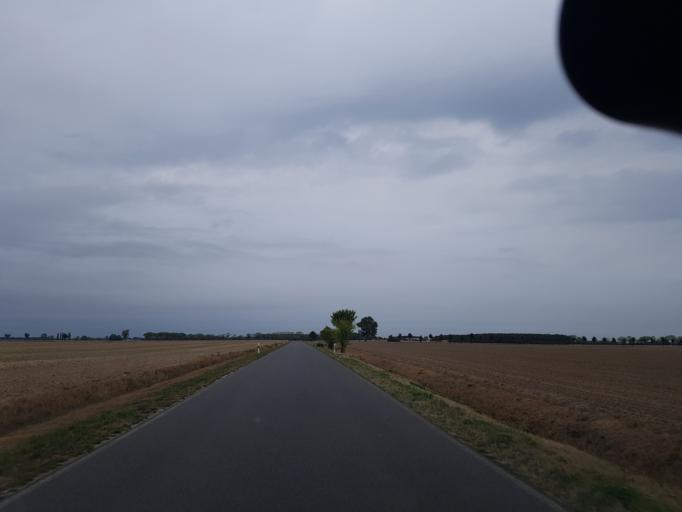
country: DE
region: Saxony-Anhalt
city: Prettin
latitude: 51.7147
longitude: 12.8946
